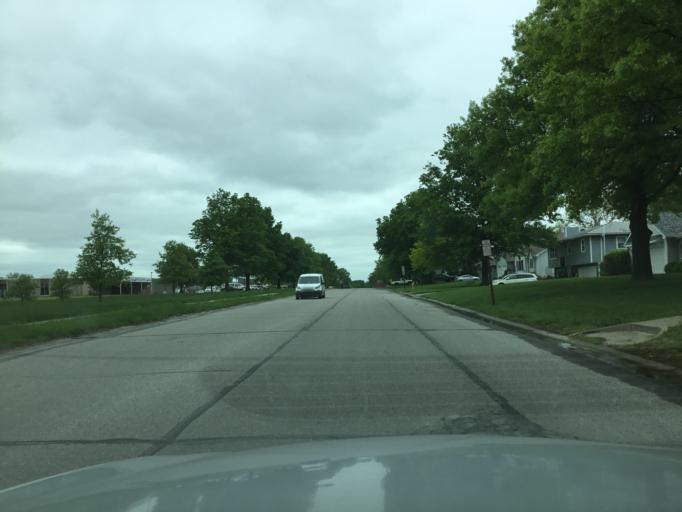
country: US
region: Kansas
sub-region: Franklin County
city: Ottawa
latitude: 38.5941
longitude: -95.2770
